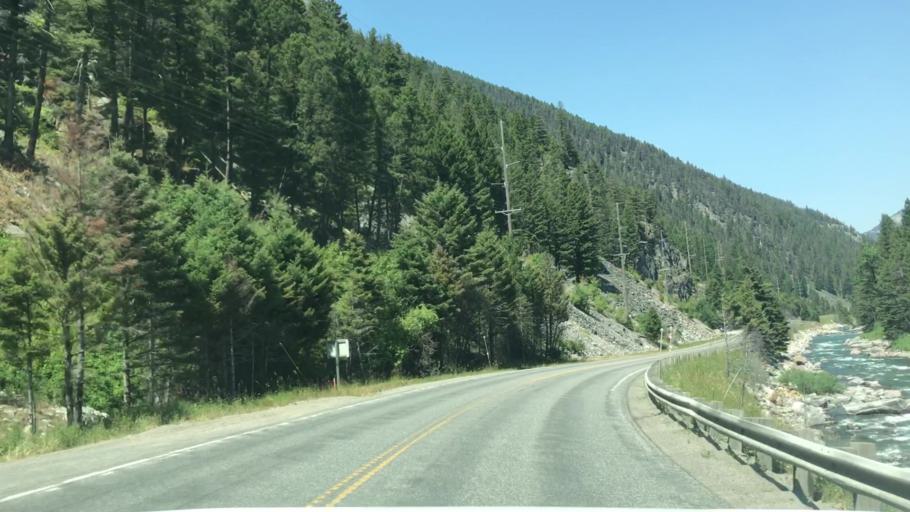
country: US
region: Montana
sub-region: Gallatin County
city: Big Sky
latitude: 45.4157
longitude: -111.2325
